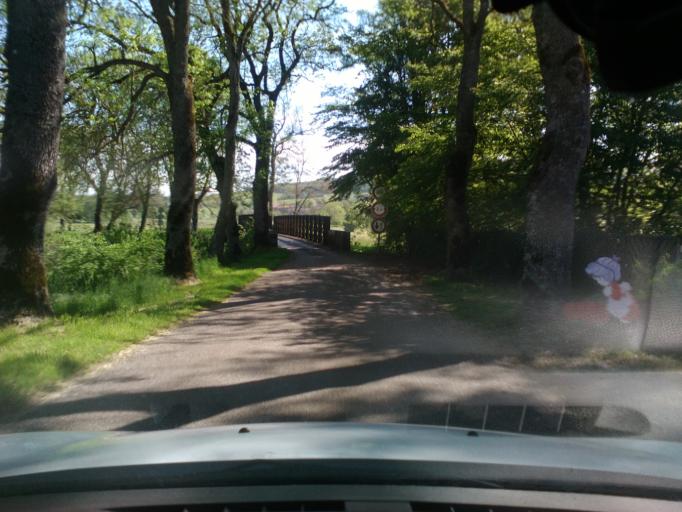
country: FR
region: Lorraine
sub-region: Departement des Vosges
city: Mirecourt
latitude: 48.3246
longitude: 6.1447
